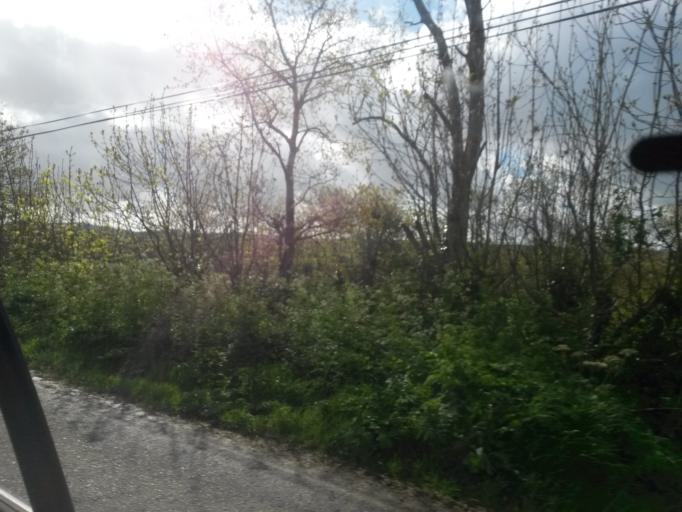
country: IE
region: Leinster
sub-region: Loch Garman
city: Ferns
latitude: 52.5961
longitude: -6.4781
